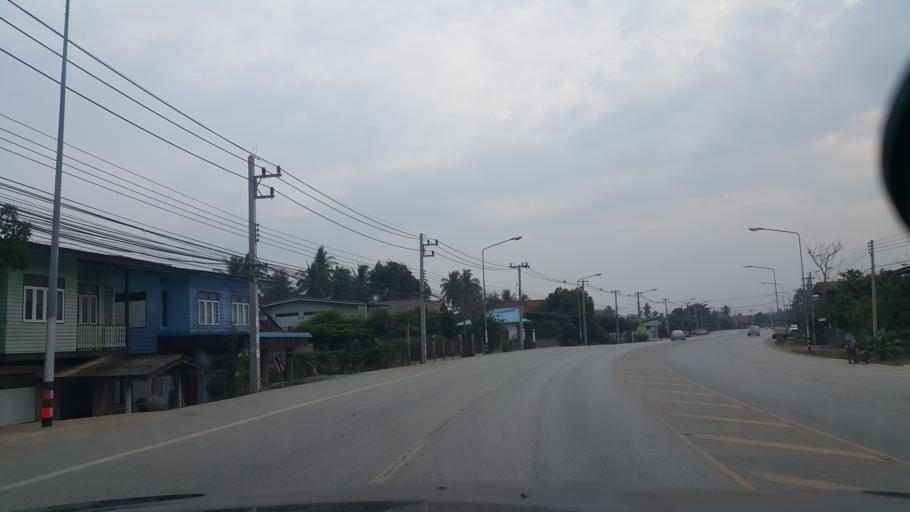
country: TH
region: Sukhothai
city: Si Samrong
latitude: 17.1610
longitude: 99.8674
